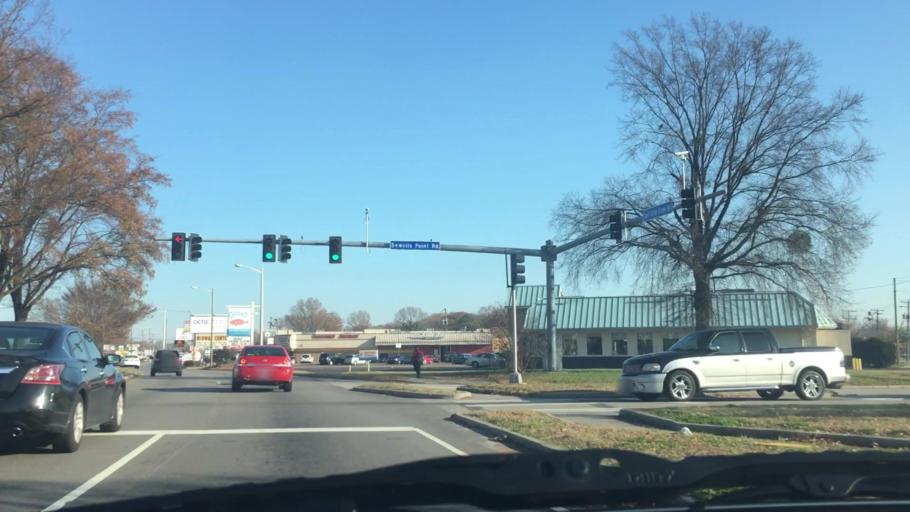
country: US
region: Virginia
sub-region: City of Norfolk
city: Norfolk
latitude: 36.9153
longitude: -76.2507
